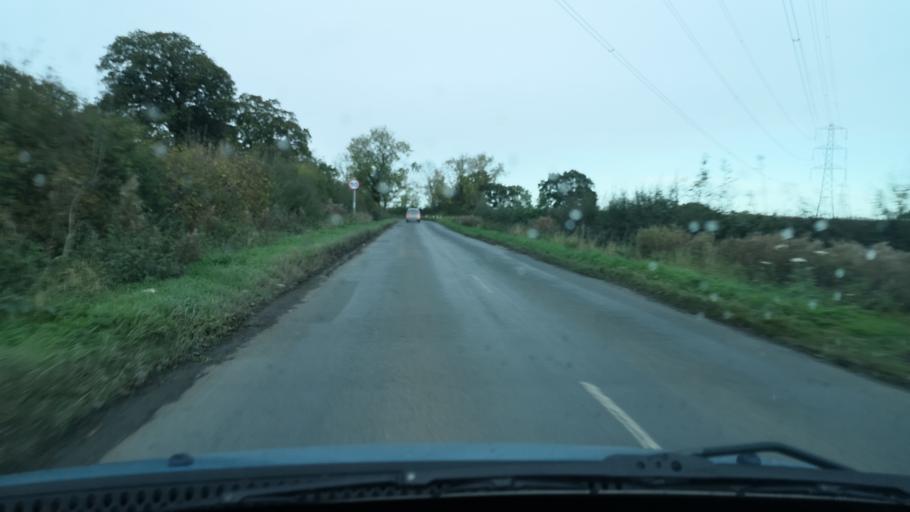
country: GB
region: England
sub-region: Doncaster
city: Moss
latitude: 53.6221
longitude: -1.0808
